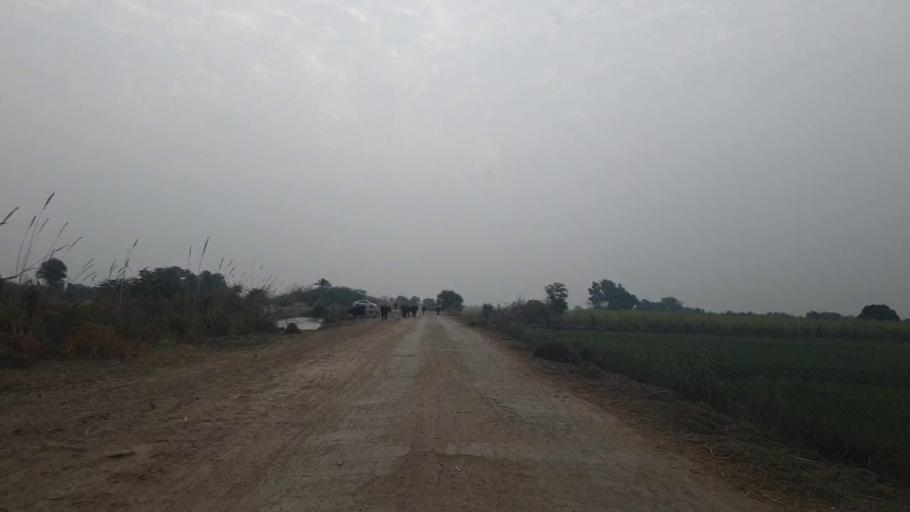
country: PK
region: Sindh
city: Tando Adam
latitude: 25.7254
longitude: 68.7260
